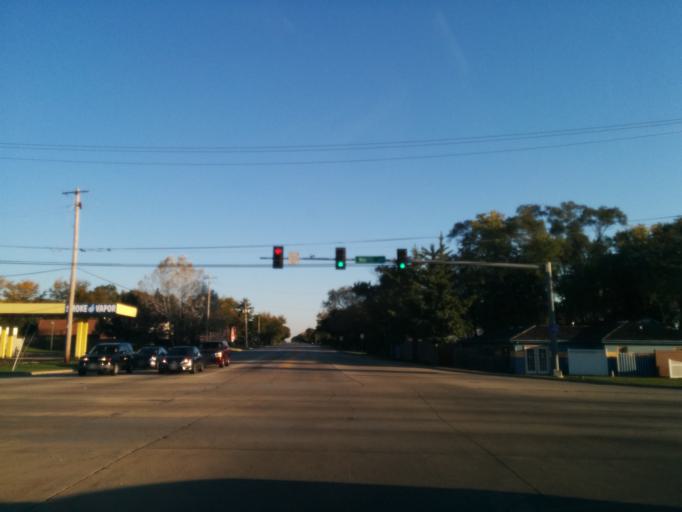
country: US
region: Illinois
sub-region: DuPage County
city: Carol Stream
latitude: 41.9075
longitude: -88.1505
